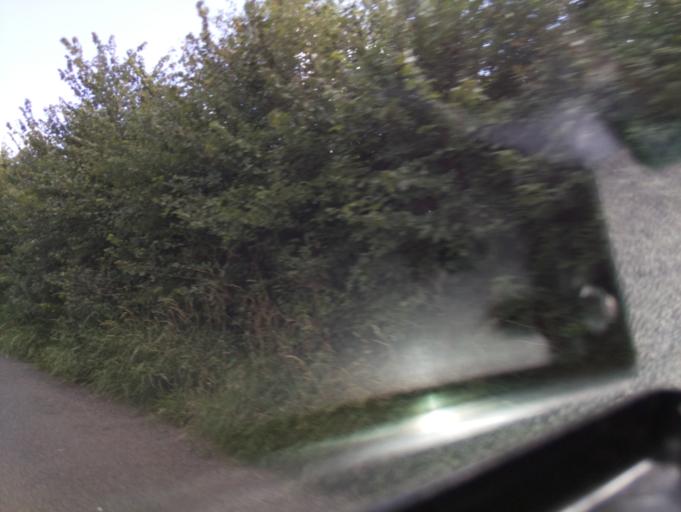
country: GB
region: England
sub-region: Gloucestershire
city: Newent
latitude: 51.8619
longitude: -2.3511
